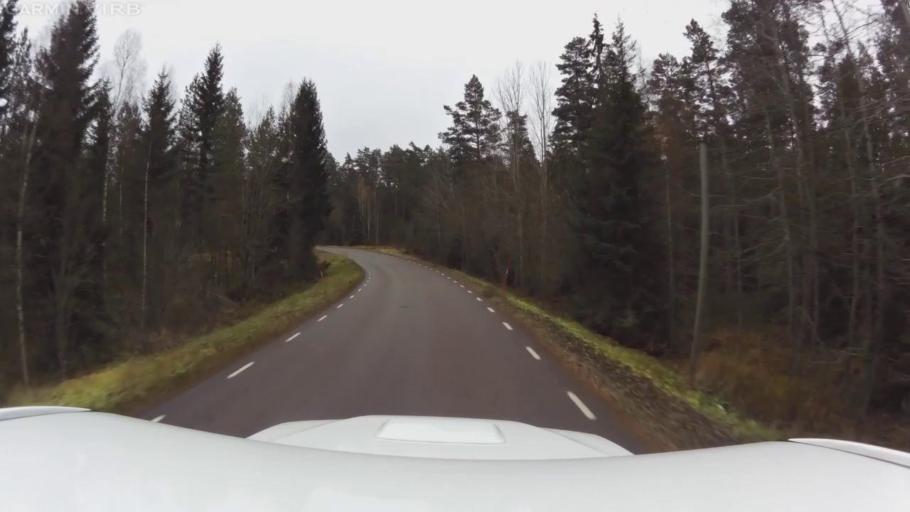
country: SE
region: OEstergoetland
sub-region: Mjolby Kommun
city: Mantorp
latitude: 58.1407
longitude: 15.4054
